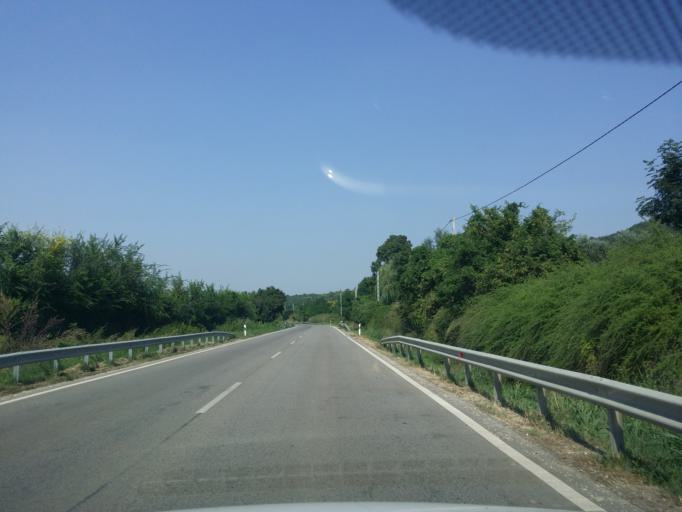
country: HU
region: Tolna
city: Pincehely
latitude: 46.6998
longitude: 18.4666
